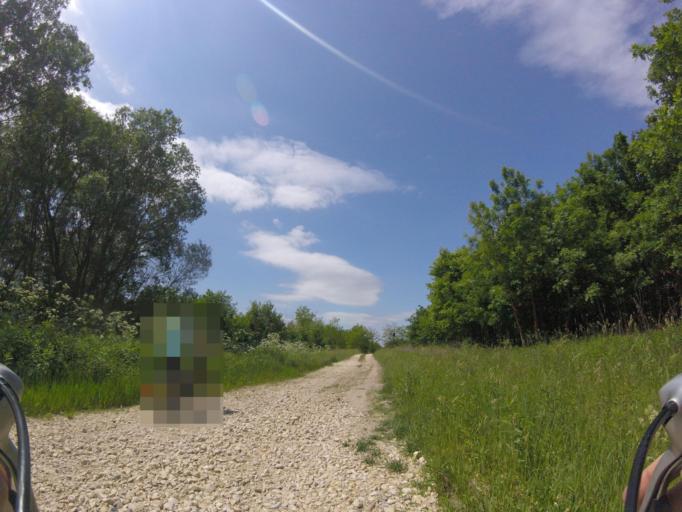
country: HU
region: Veszprem
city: Devecser
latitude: 47.1439
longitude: 17.4444
